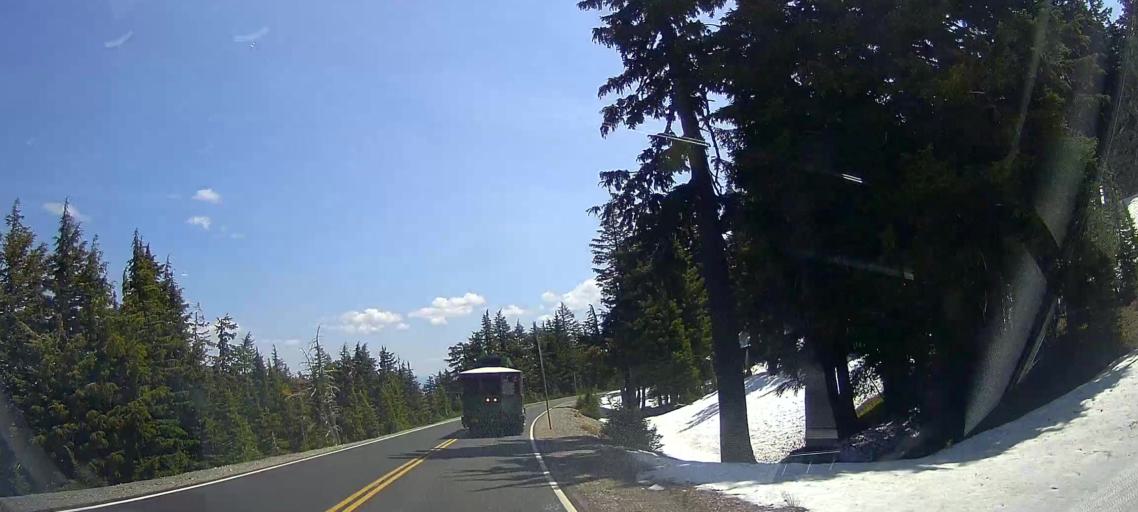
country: US
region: Oregon
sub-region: Jackson County
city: Shady Cove
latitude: 42.9822
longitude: -122.1349
